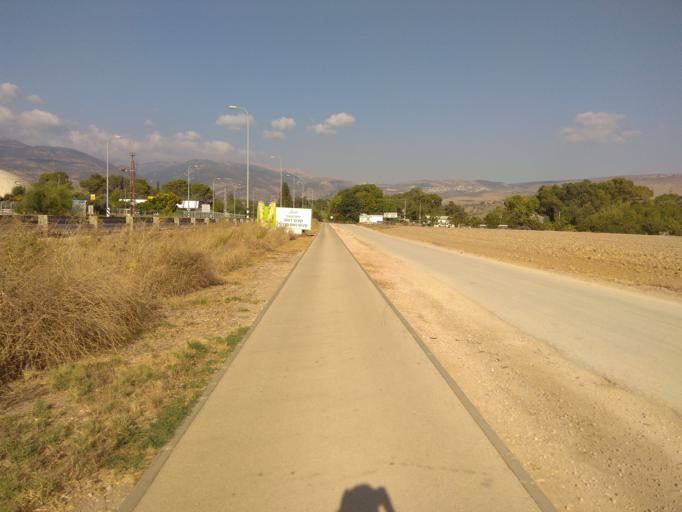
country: IL
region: Northern District
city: Qiryat Shemona
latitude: 33.2253
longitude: 35.6352
